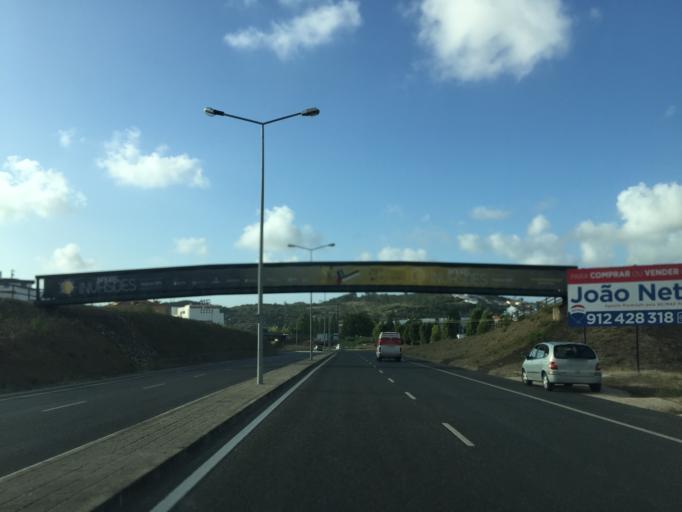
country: PT
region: Lisbon
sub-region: Torres Vedras
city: Torres Vedras
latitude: 39.0888
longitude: -9.2642
